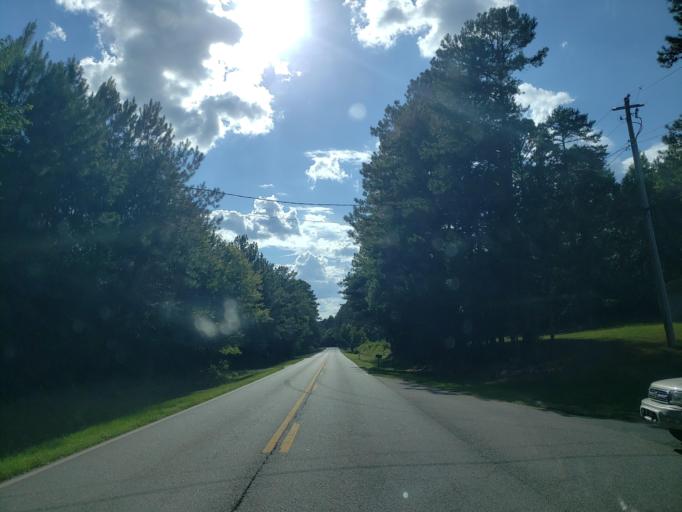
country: US
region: Georgia
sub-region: Bartow County
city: Euharlee
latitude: 34.1765
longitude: -84.9993
